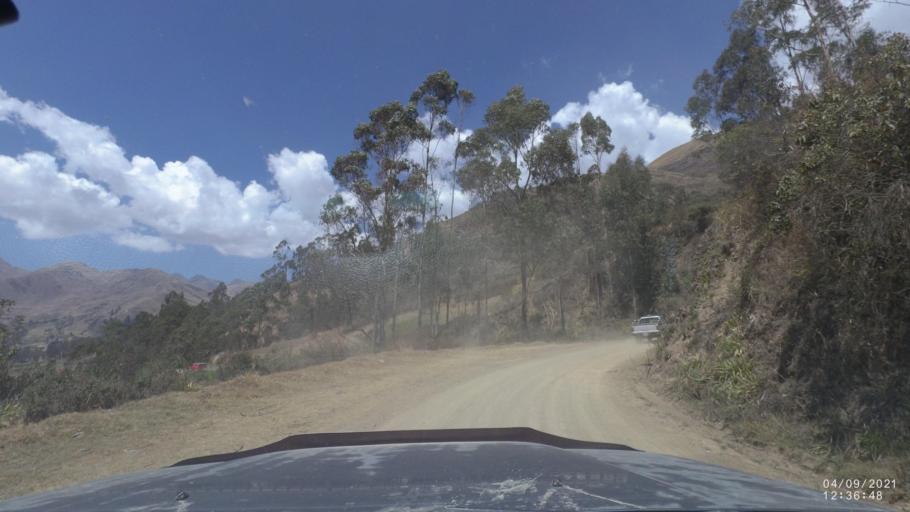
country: BO
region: Cochabamba
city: Colchani
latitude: -17.2257
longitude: -66.5057
